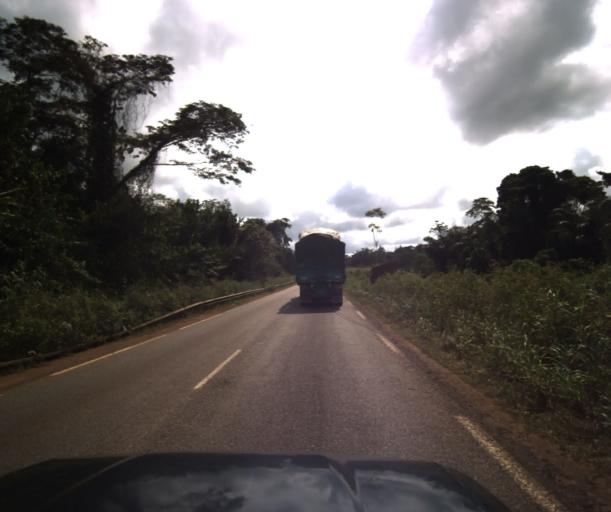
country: CM
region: Littoral
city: Edea
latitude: 3.8034
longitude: 10.2463
